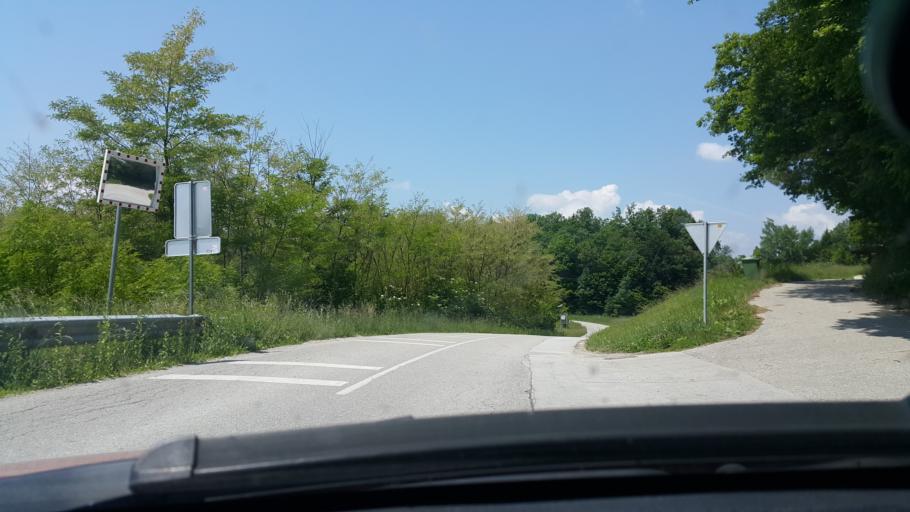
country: SI
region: Novo Mesto
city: Novo Mesto
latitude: 45.7642
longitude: 15.1629
